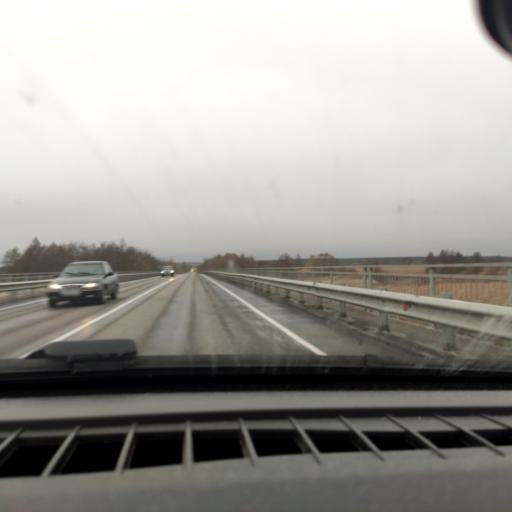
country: RU
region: Voronezj
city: Ostrogozhsk
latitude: 51.0312
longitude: 38.9862
